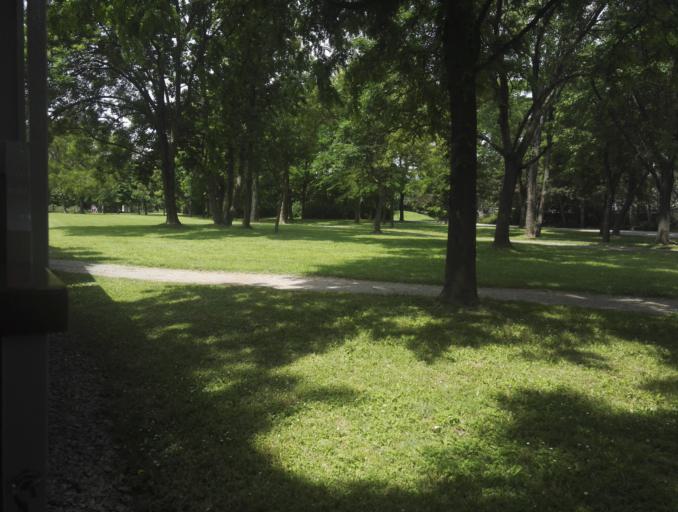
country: AT
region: Vienna
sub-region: Wien Stadt
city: Vienna
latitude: 48.2399
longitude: 16.4066
